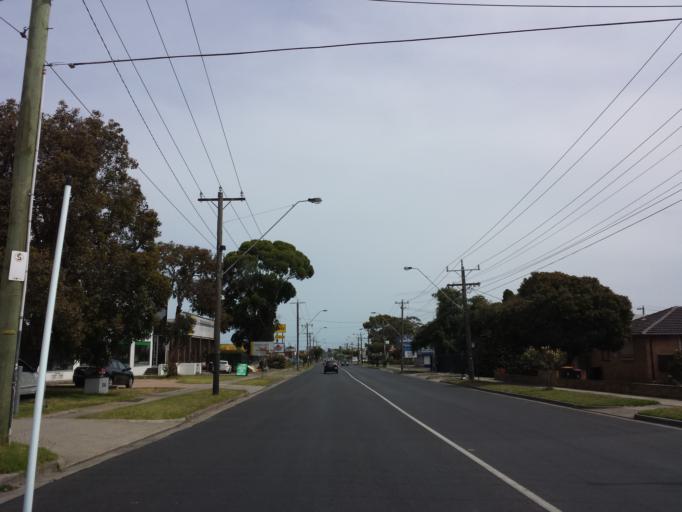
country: AU
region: Victoria
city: Highett
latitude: -37.9422
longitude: 145.0601
